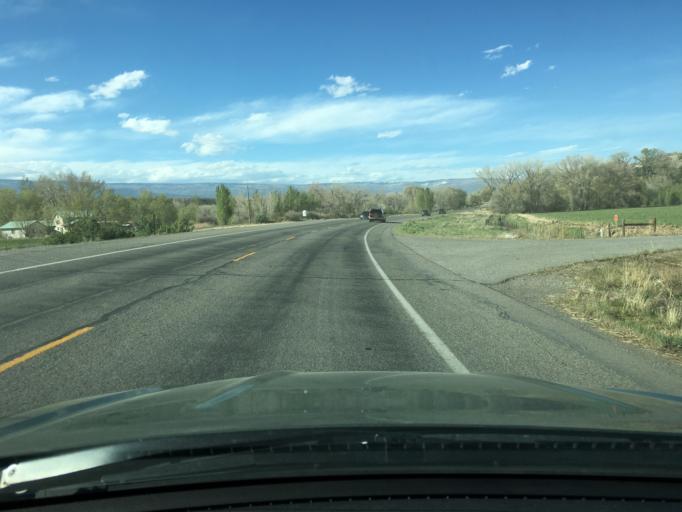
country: US
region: Colorado
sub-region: Delta County
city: Orchard City
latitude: 38.7694
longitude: -108.0040
